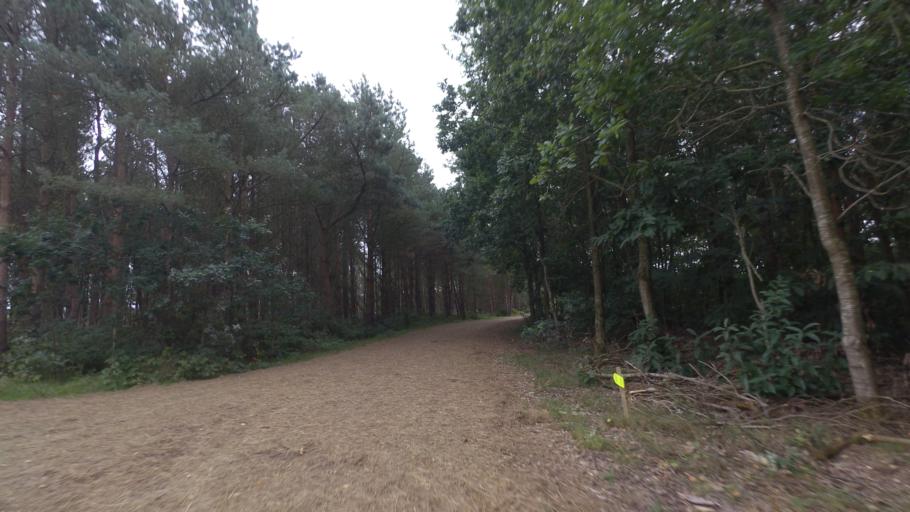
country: NL
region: Friesland
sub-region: Gemeente Ameland
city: Nes
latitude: 53.4536
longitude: 5.7854
